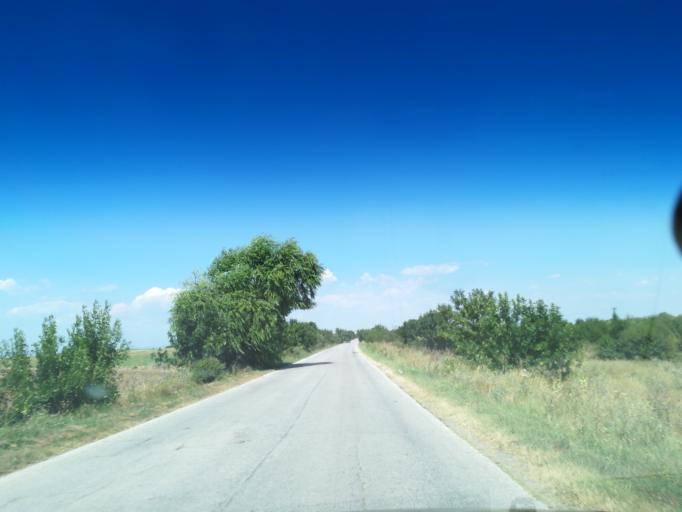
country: BG
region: Plovdiv
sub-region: Obshtina Sadovo
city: Sadovo
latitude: 42.0480
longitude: 25.1427
